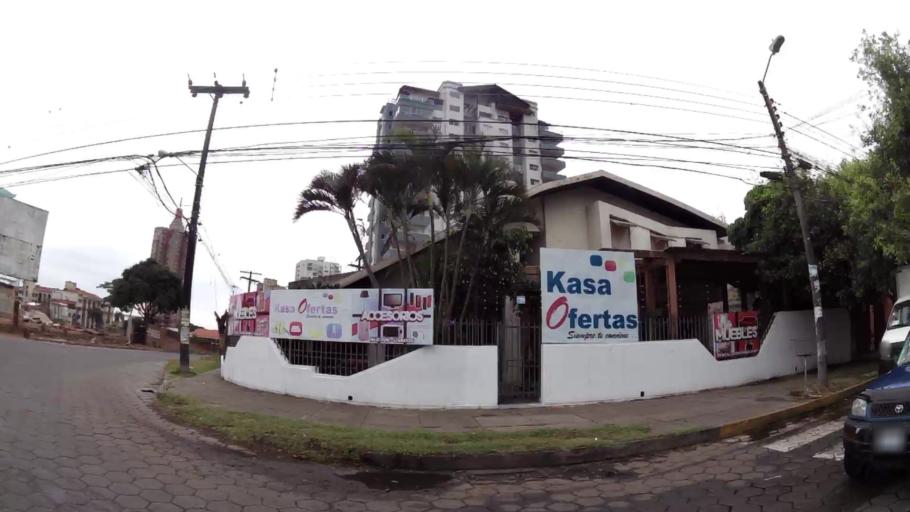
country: BO
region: Santa Cruz
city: Santa Cruz de la Sierra
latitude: -17.7744
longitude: -63.1847
